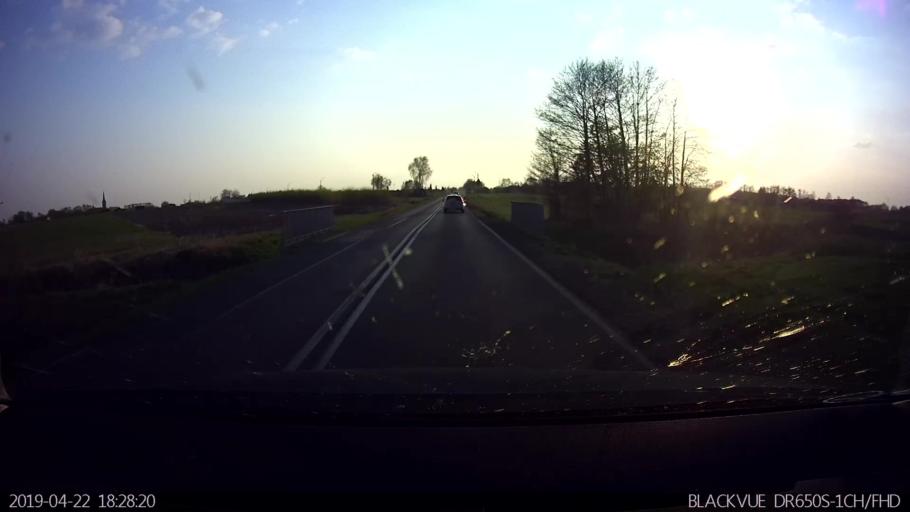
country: PL
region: Masovian Voivodeship
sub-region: Powiat wolominski
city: Tluszcz
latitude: 52.4585
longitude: 21.4752
